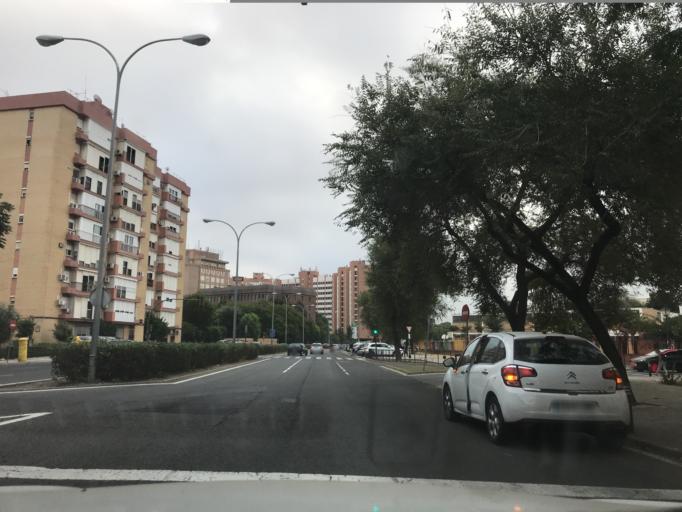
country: ES
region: Andalusia
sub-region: Provincia de Sevilla
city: San Juan de Aznalfarache
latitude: 37.3761
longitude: -6.0121
